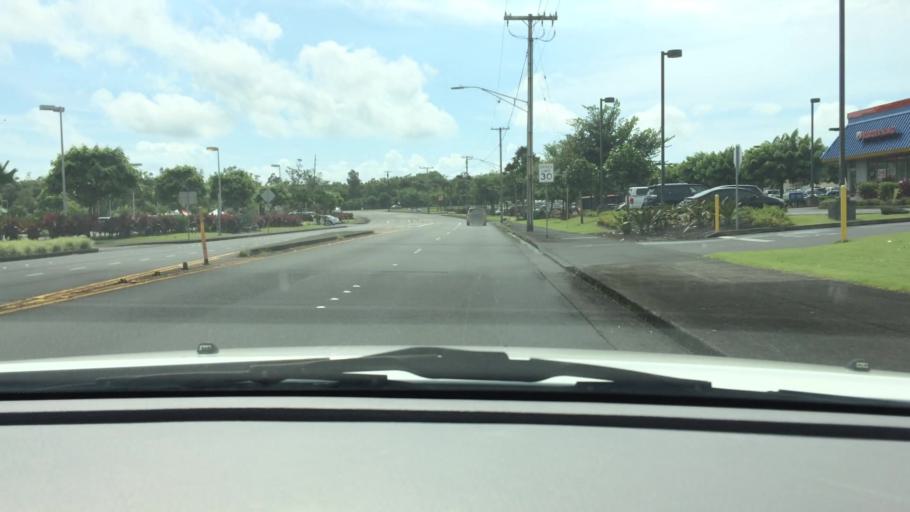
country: US
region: Hawaii
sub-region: Hawaii County
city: Hilo
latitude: 19.6992
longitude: -155.0612
